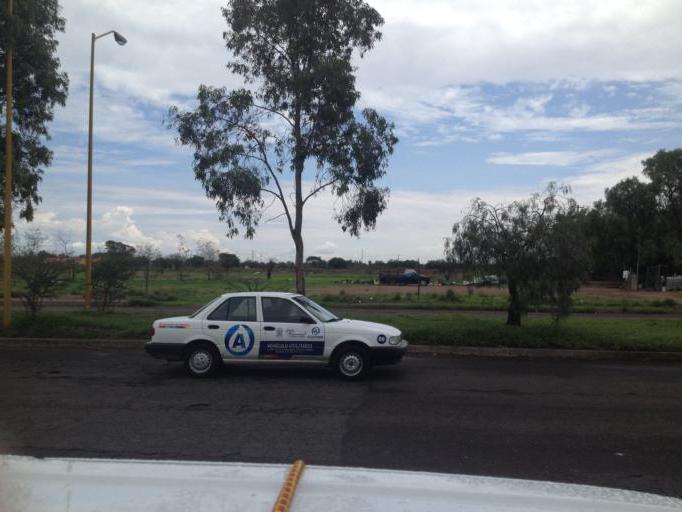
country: MX
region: Aguascalientes
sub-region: Aguascalientes
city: La Loma de los Negritos
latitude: 21.8439
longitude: -102.3280
